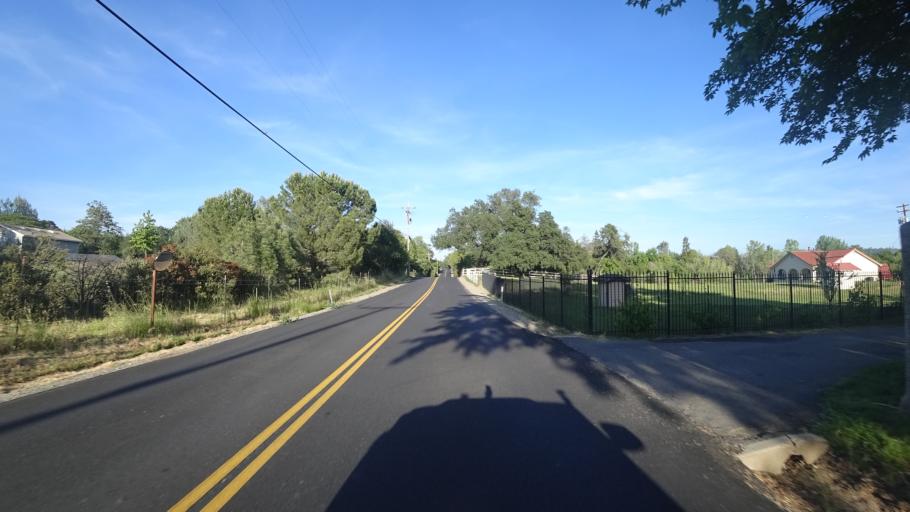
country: US
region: California
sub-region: Placer County
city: Lincoln
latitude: 38.9123
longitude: -121.2133
